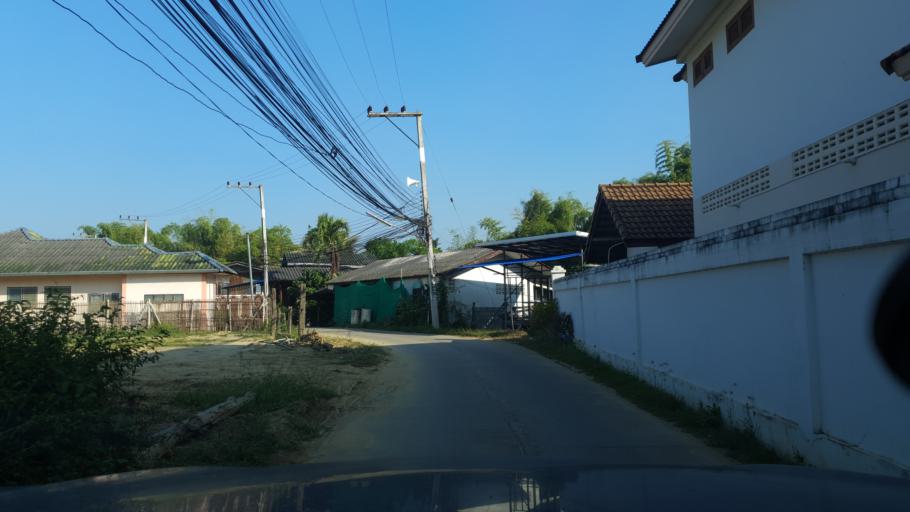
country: TH
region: Chiang Mai
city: Saraphi
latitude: 18.7208
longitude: 99.0705
